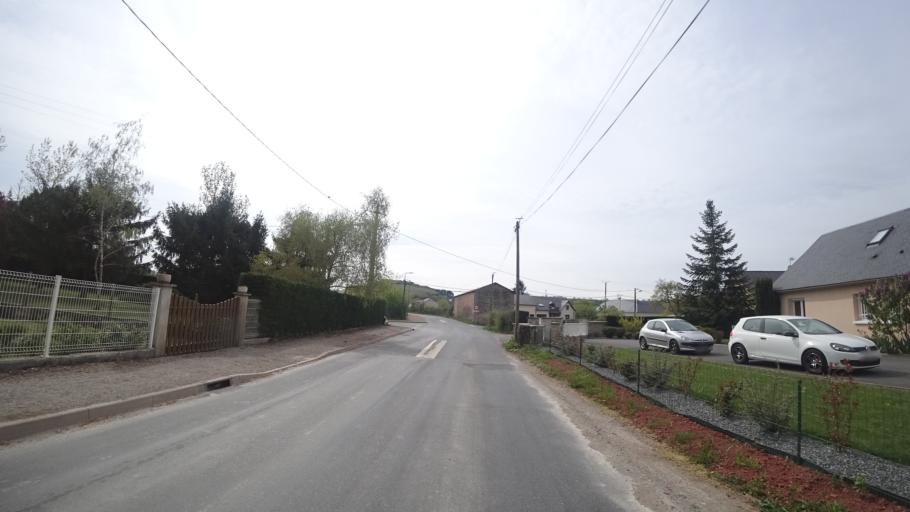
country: FR
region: Midi-Pyrenees
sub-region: Departement de l'Aveyron
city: Sebazac-Concoures
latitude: 44.3792
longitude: 2.6036
